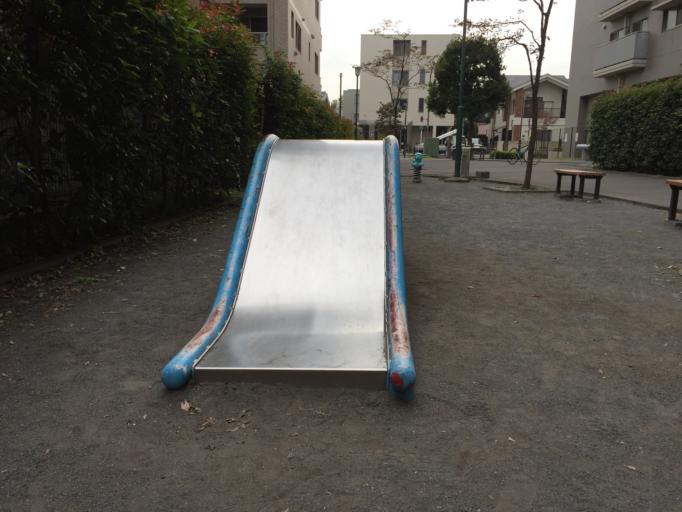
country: JP
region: Tokyo
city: Kokubunji
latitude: 35.6705
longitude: 139.4829
